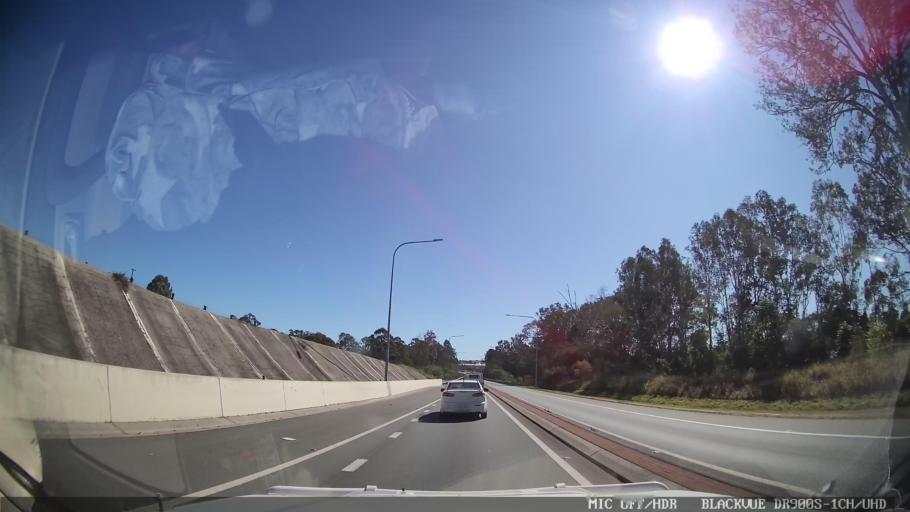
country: AU
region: Queensland
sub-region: Gympie Regional Council
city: Monkland
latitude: -26.2353
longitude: 152.6987
